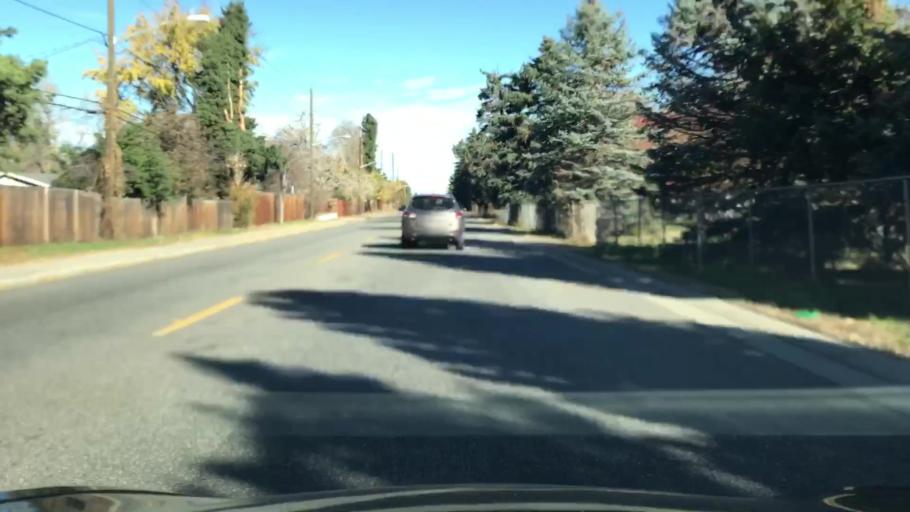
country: US
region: Colorado
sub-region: Arapahoe County
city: Glendale
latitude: 39.7051
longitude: -104.9034
